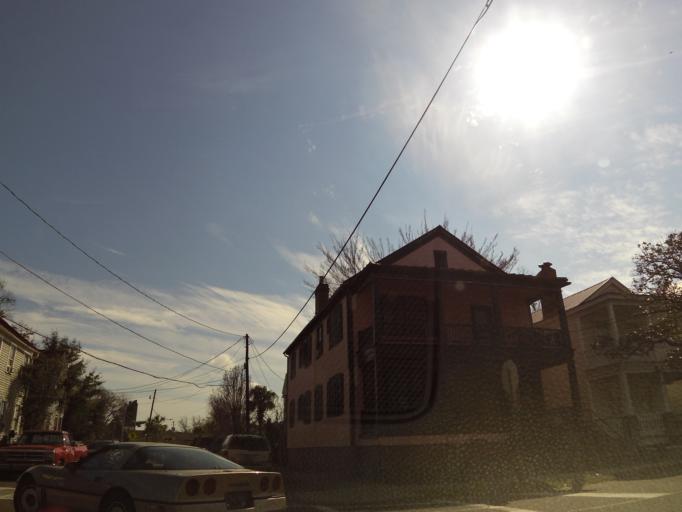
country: US
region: South Carolina
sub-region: Charleston County
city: Charleston
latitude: 32.7953
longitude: -79.9471
